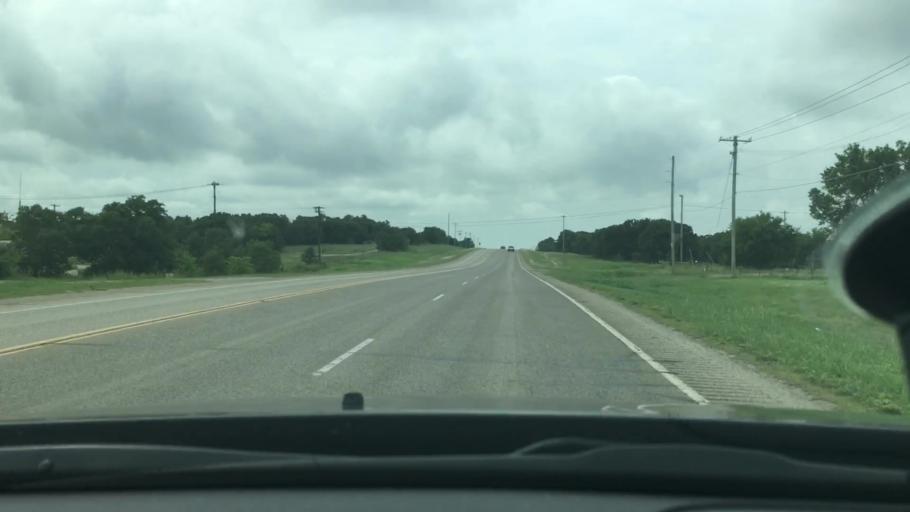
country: US
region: Oklahoma
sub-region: Carter County
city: Healdton
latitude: 34.2029
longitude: -97.4749
